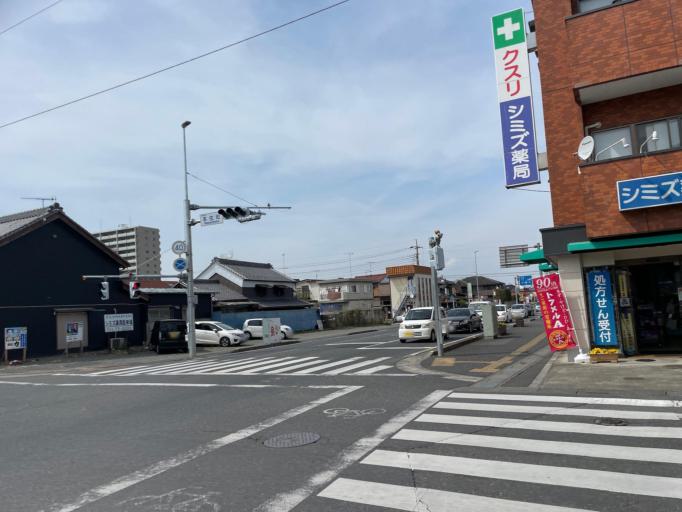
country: JP
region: Saitama
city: Fukayacho
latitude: 36.1951
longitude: 139.2854
